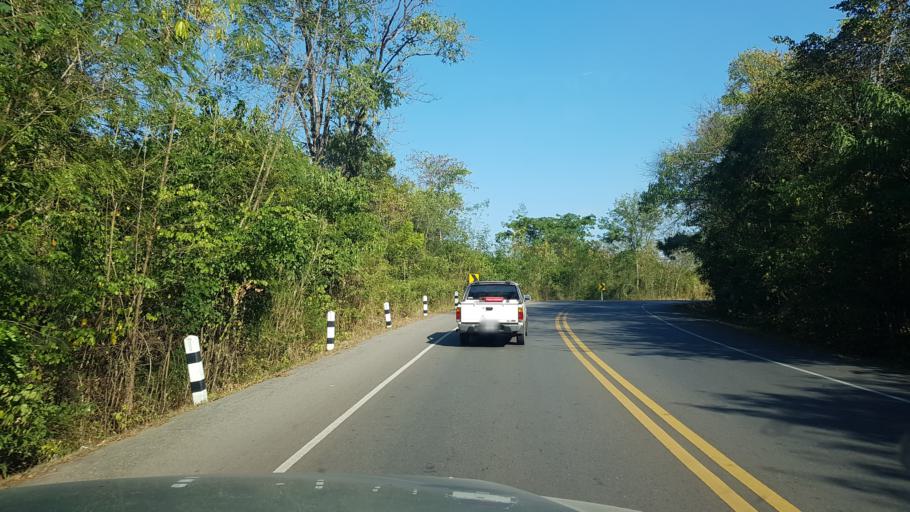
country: TH
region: Phetchabun
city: Phetchabun
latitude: 16.5348
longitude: 101.1083
